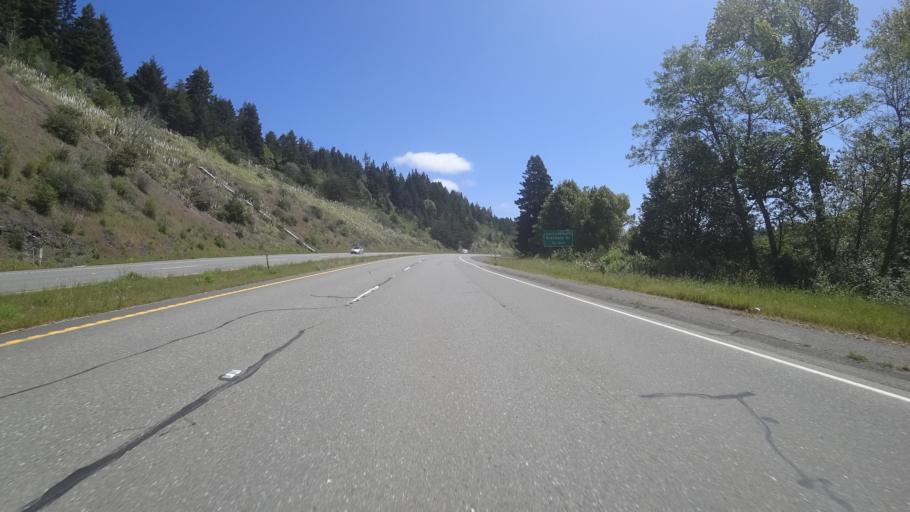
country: US
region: California
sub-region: Humboldt County
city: Arcata
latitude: 40.9095
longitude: -124.0523
